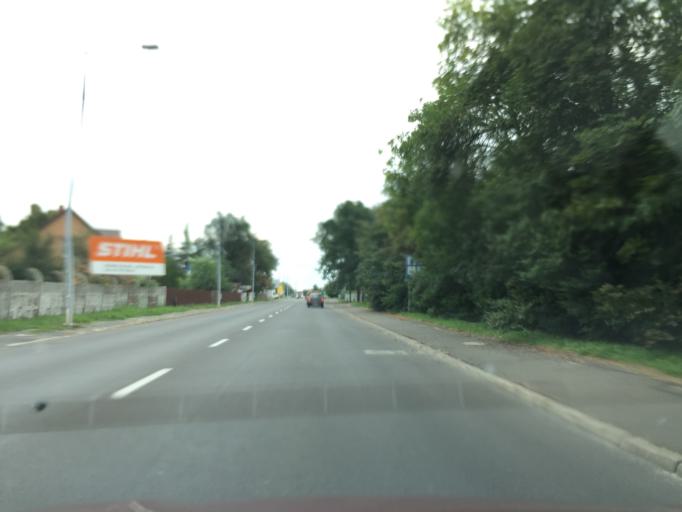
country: PL
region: Greater Poland Voivodeship
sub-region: Kalisz
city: Kalisz
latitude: 51.7821
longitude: 18.0895
